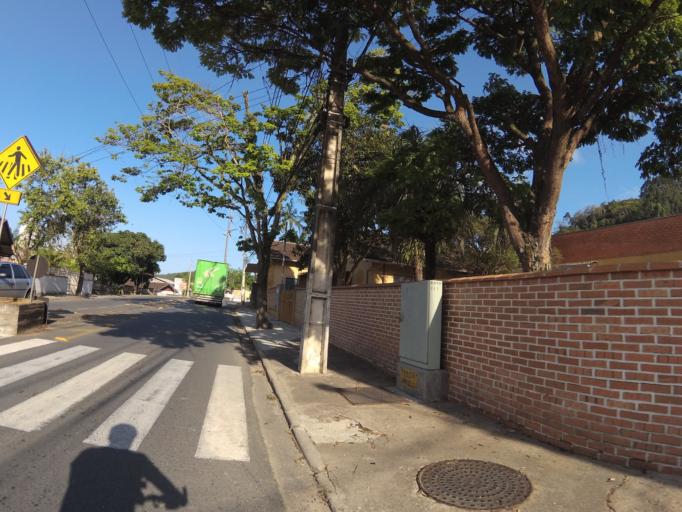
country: BR
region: Santa Catarina
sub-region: Blumenau
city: Blumenau
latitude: -26.9238
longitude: -49.1076
